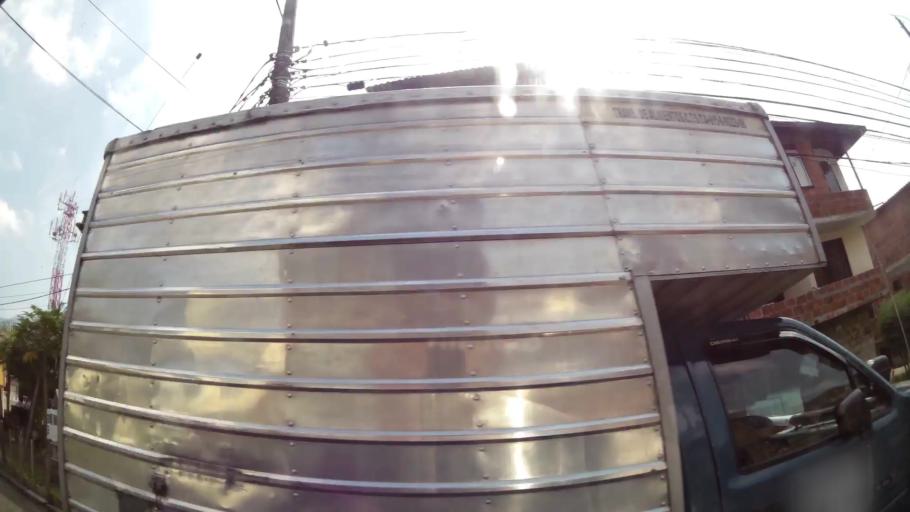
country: CO
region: Antioquia
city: La Estrella
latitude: 6.1750
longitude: -75.6383
